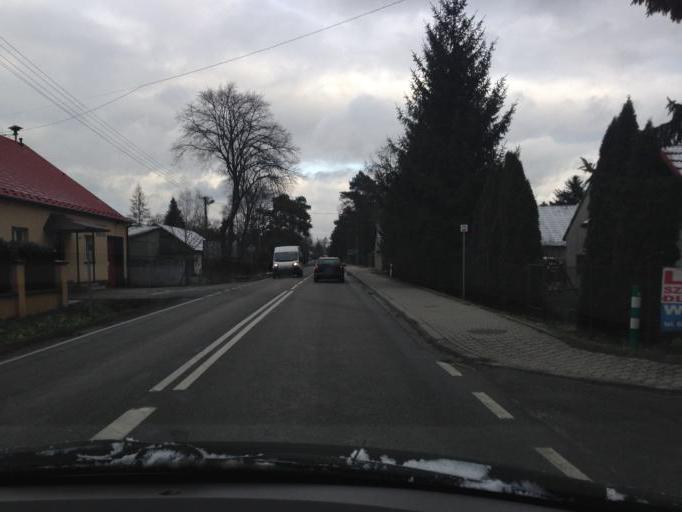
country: PL
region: Lesser Poland Voivodeship
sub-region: Powiat wielicki
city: Gdow
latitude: 49.9019
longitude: 20.1435
